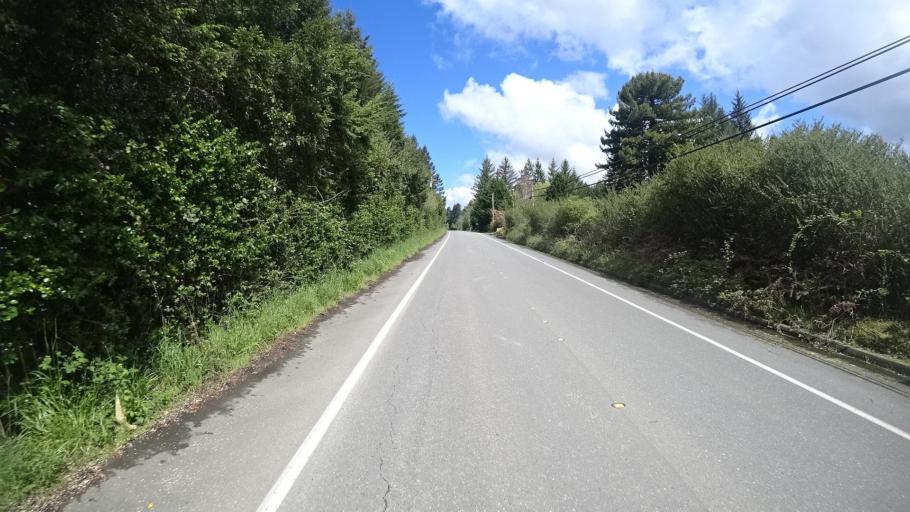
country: US
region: California
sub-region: Humboldt County
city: McKinleyville
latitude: 40.9494
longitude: -124.0318
